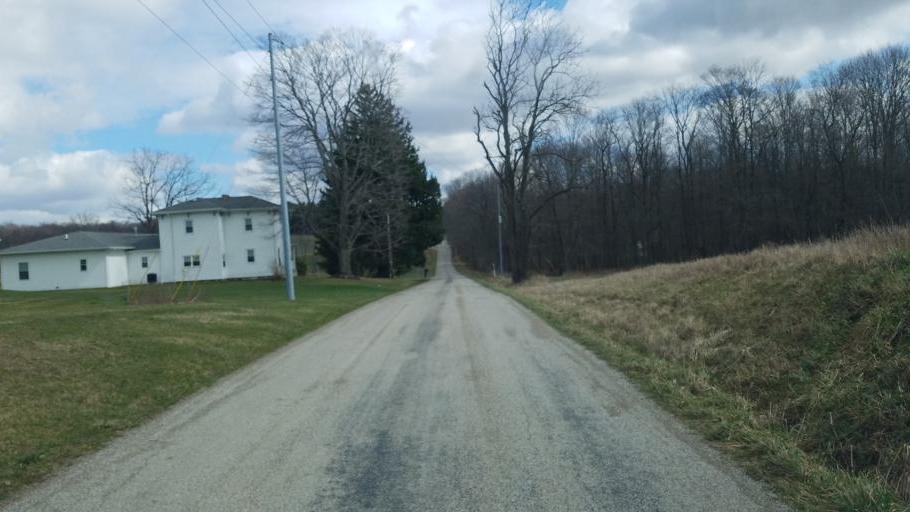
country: US
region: Ohio
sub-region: Sandusky County
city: Bellville
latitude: 40.5655
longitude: -82.4887
